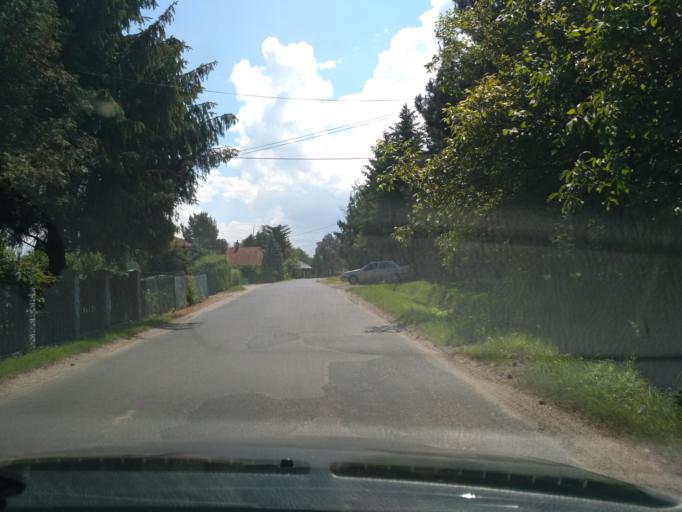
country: PL
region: Subcarpathian Voivodeship
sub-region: Powiat lancucki
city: Sonina
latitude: 50.0601
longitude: 22.2672
